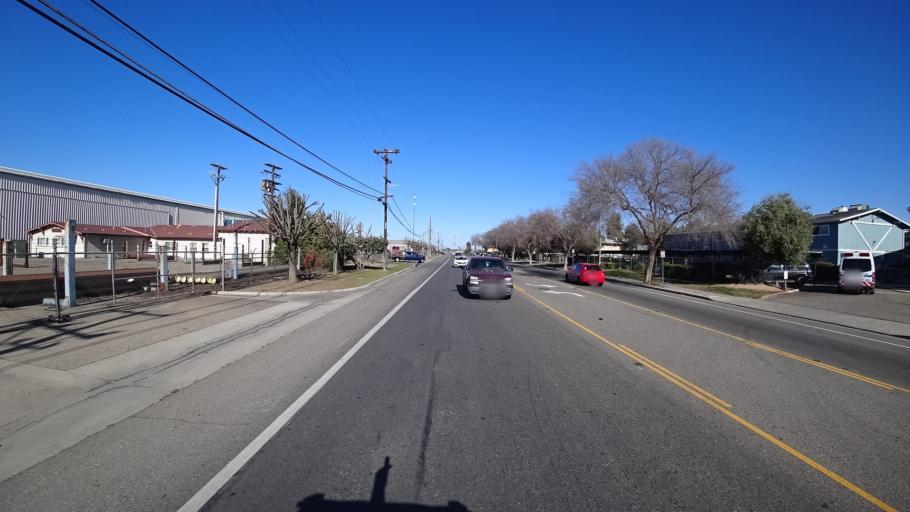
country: US
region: California
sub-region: Fresno County
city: West Park
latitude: 36.7743
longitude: -119.8367
